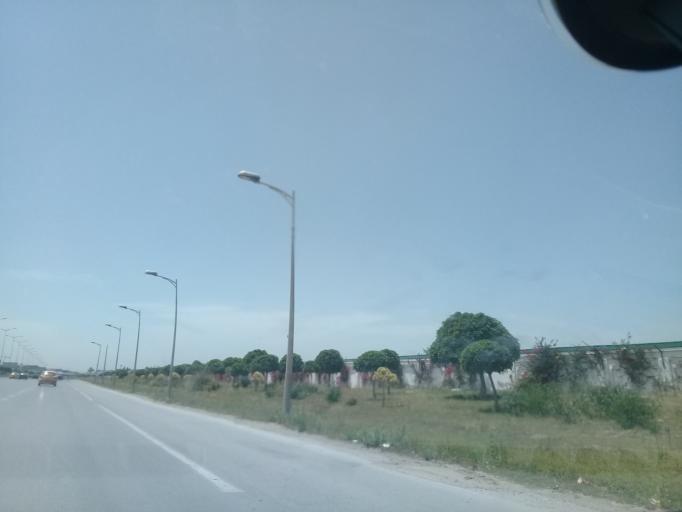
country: TN
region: Ariana
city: Ariana
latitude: 36.8435
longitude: 10.2492
